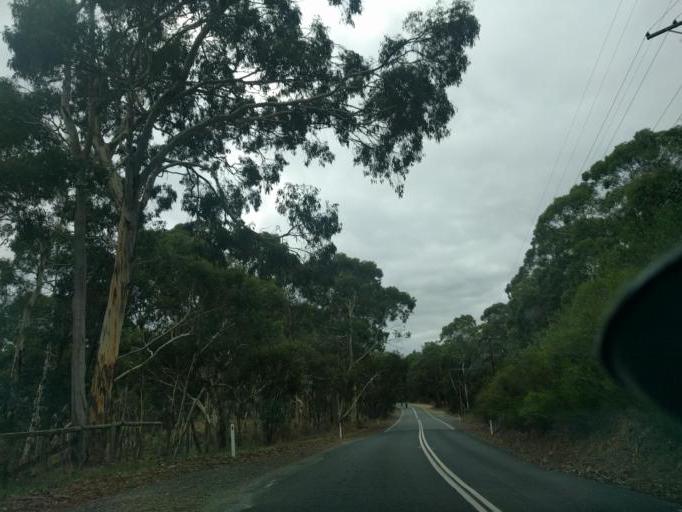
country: AU
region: South Australia
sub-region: Adelaide Hills
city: Stirling
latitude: -35.0561
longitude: 138.7608
